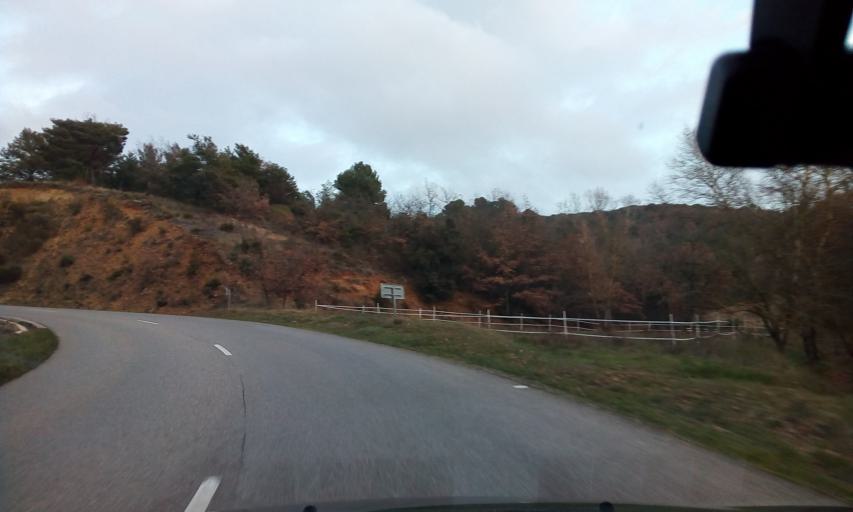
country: FR
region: Provence-Alpes-Cote d'Azur
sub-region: Departement des Alpes-de-Haute-Provence
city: Greoux-les-Bains
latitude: 43.7887
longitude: 5.8601
